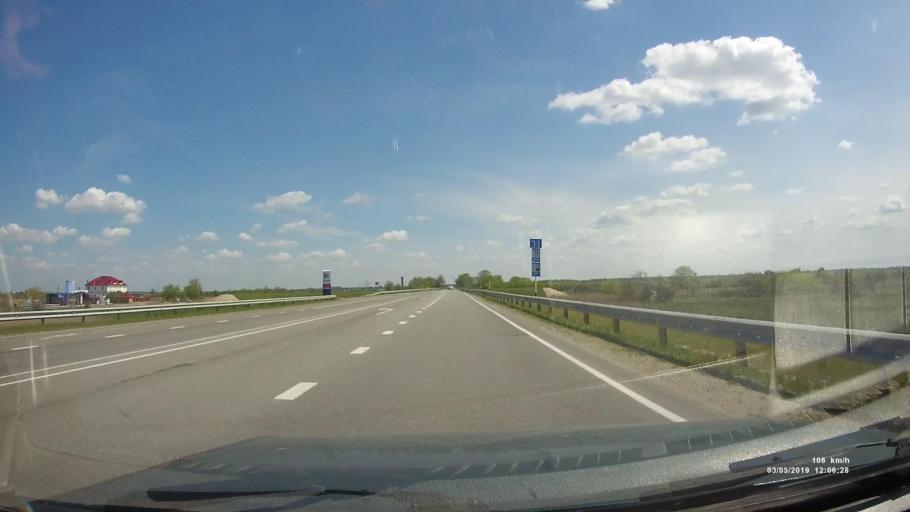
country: RU
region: Rostov
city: Bagayevskaya
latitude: 47.2857
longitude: 40.4525
